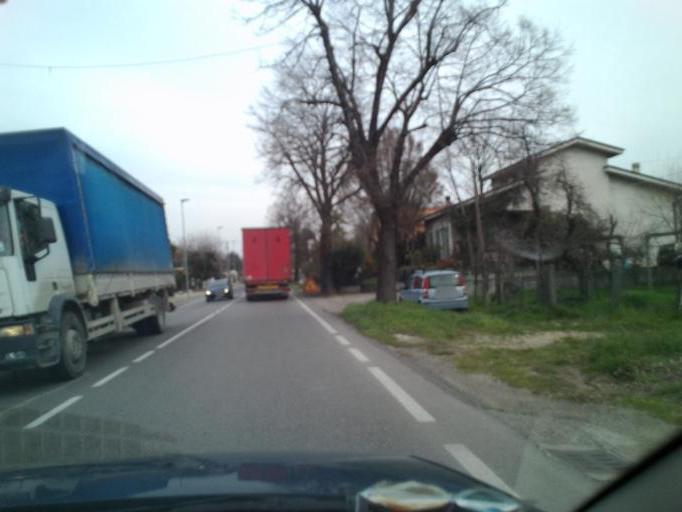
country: IT
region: Veneto
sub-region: Provincia di Verona
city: Mozzecane
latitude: 45.3009
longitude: 10.8113
